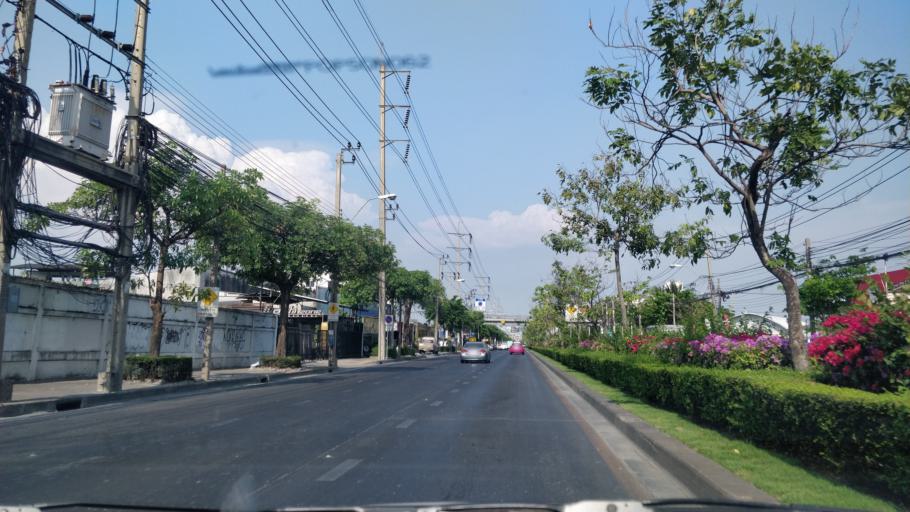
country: TH
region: Bangkok
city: Suan Luang
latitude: 13.7189
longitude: 100.6694
